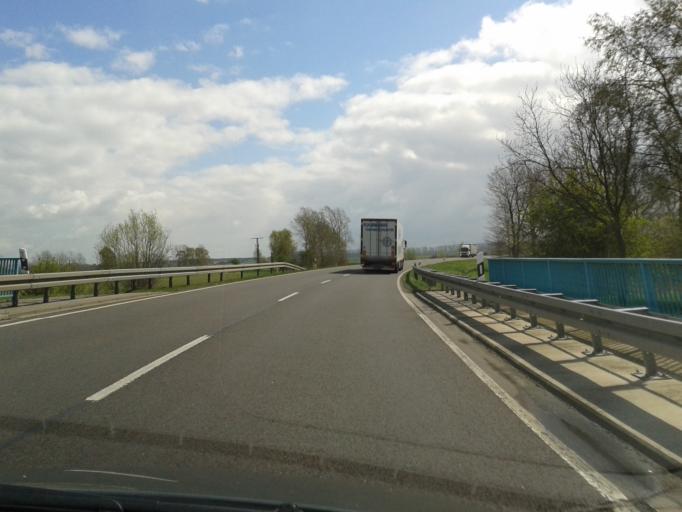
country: DE
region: Saxony-Anhalt
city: Salzwedel
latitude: 52.8667
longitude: 11.1740
